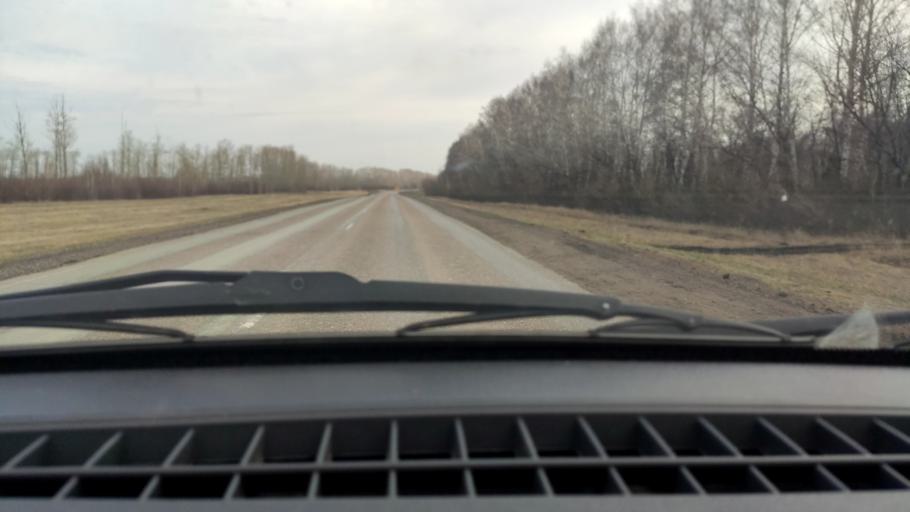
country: RU
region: Bashkortostan
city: Davlekanovo
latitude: 54.3443
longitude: 55.1746
